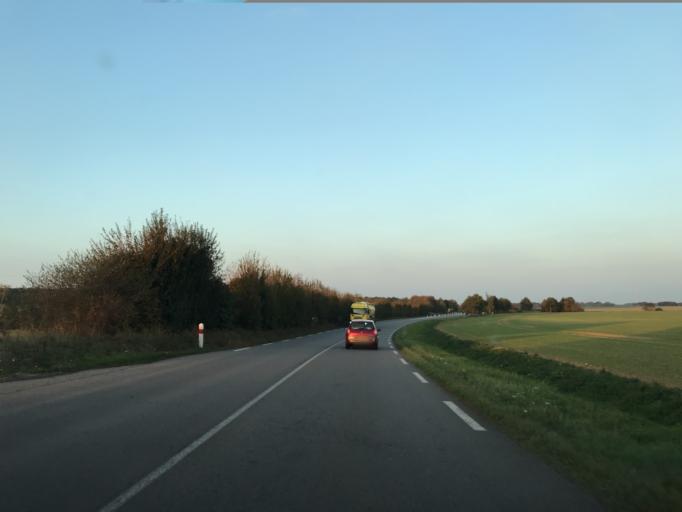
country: FR
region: Haute-Normandie
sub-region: Departement de l'Eure
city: Bourth
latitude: 48.6601
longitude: 0.7698
